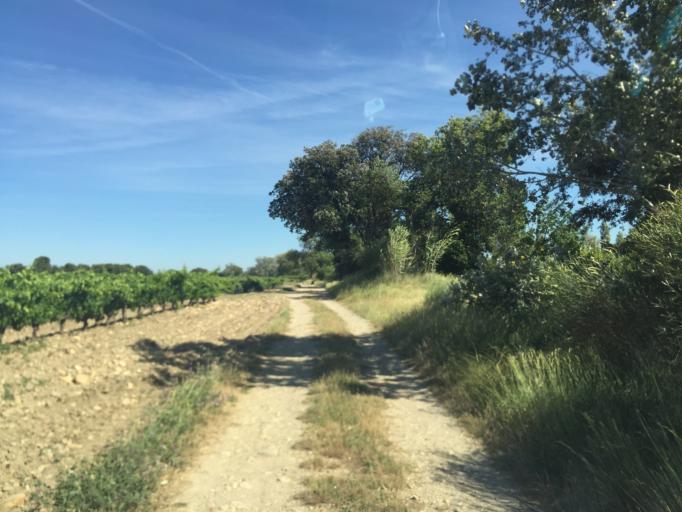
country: FR
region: Provence-Alpes-Cote d'Azur
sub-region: Departement du Vaucluse
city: Chateauneuf-du-Pape
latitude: 44.0381
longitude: 4.8306
